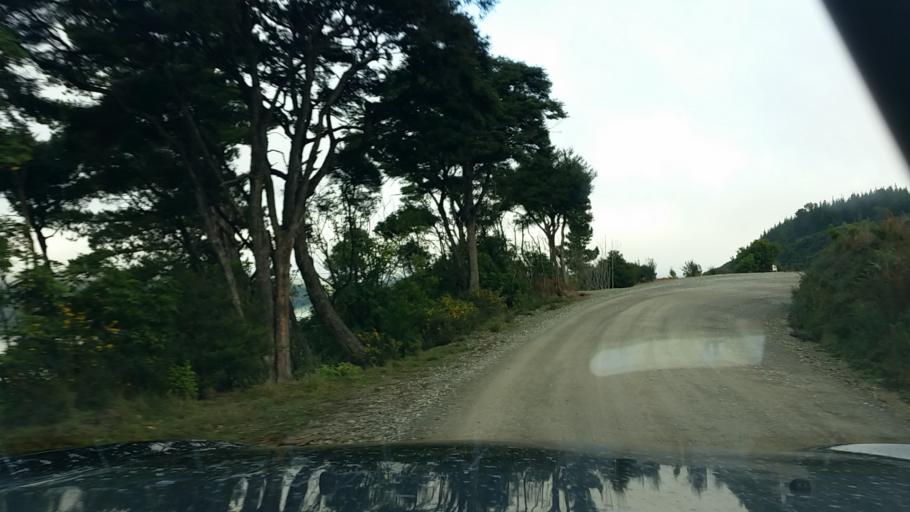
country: NZ
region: Marlborough
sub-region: Marlborough District
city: Picton
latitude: -41.1786
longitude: 174.0632
